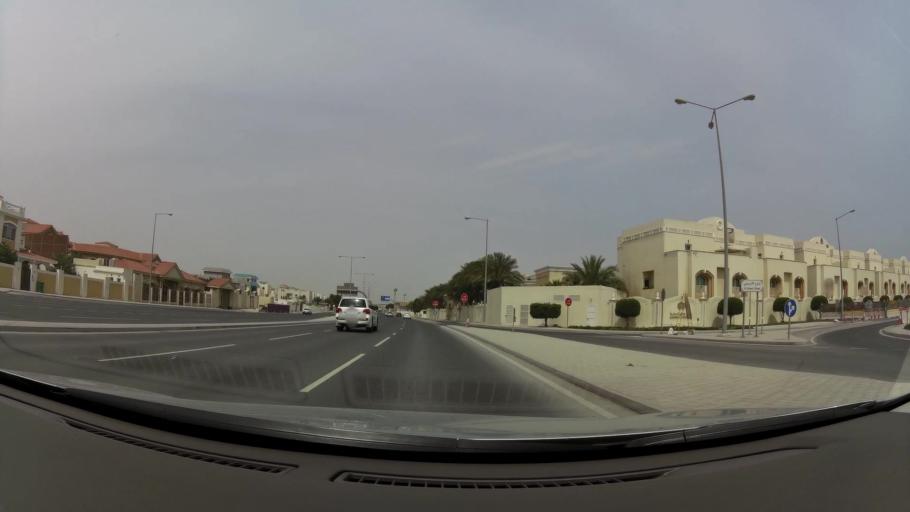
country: QA
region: Baladiyat ad Dawhah
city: Doha
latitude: 25.2582
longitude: 51.4839
